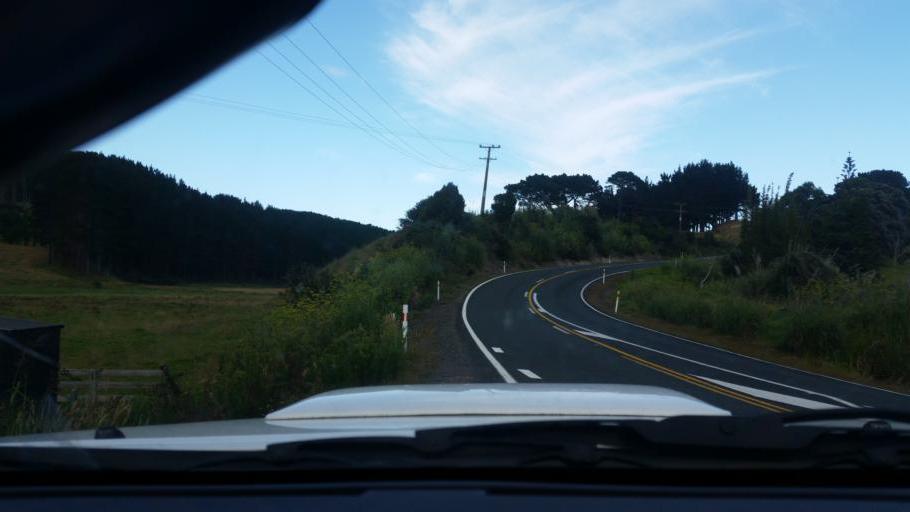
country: NZ
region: Northland
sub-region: Kaipara District
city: Dargaville
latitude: -35.8345
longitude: 173.6611
